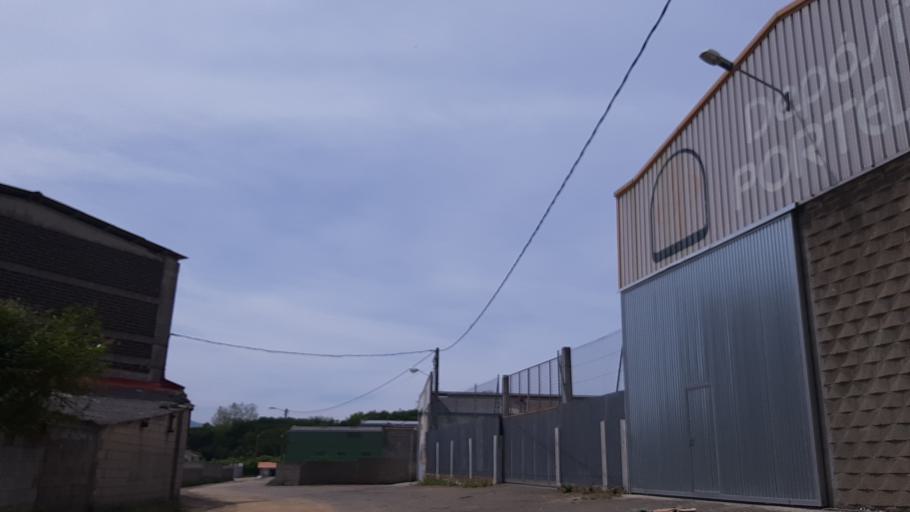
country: ES
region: Galicia
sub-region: Provincia de Pontevedra
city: A Guarda
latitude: 41.8925
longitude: -8.8514
